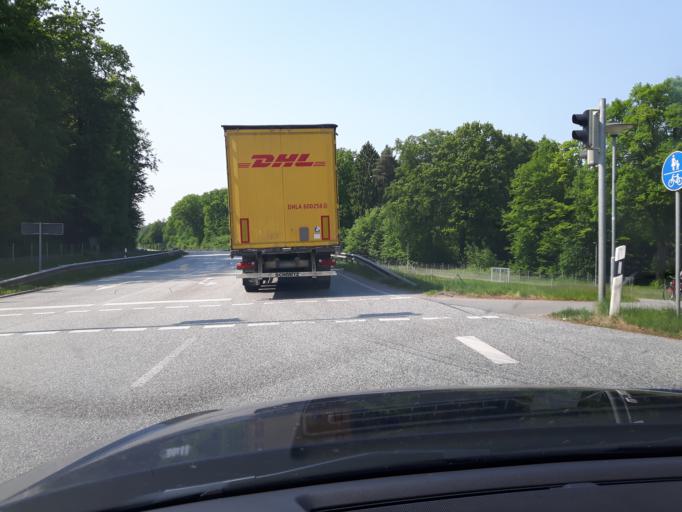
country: DE
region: Schleswig-Holstein
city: Ratekau
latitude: 53.8897
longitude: 10.7690
